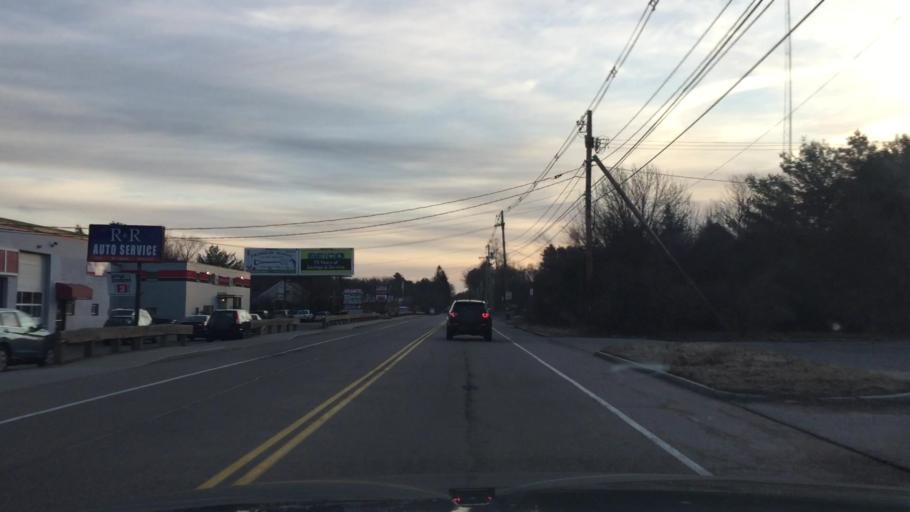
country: US
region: Massachusetts
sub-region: Norfolk County
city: Medway
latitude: 42.1587
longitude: -71.3839
